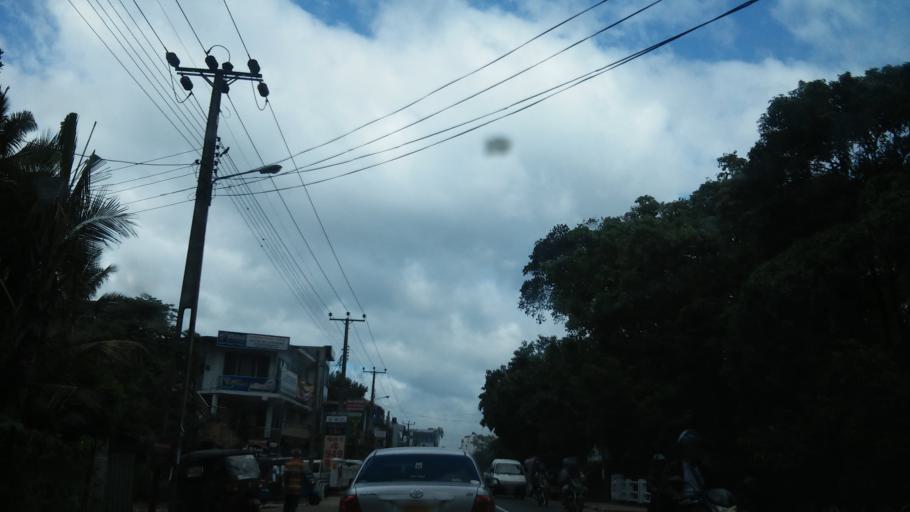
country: LK
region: Central
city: Kandy
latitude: 7.2809
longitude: 80.6221
